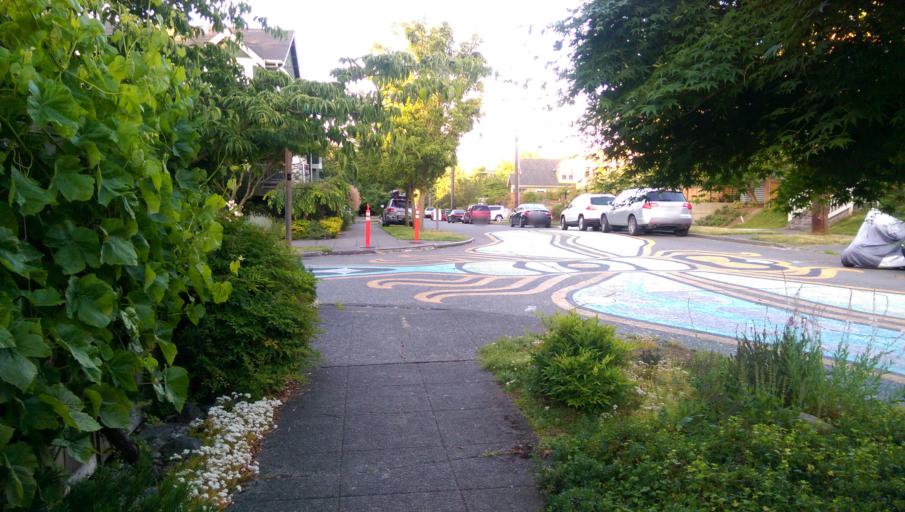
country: US
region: Washington
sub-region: King County
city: Seattle
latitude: 47.6723
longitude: -122.3246
